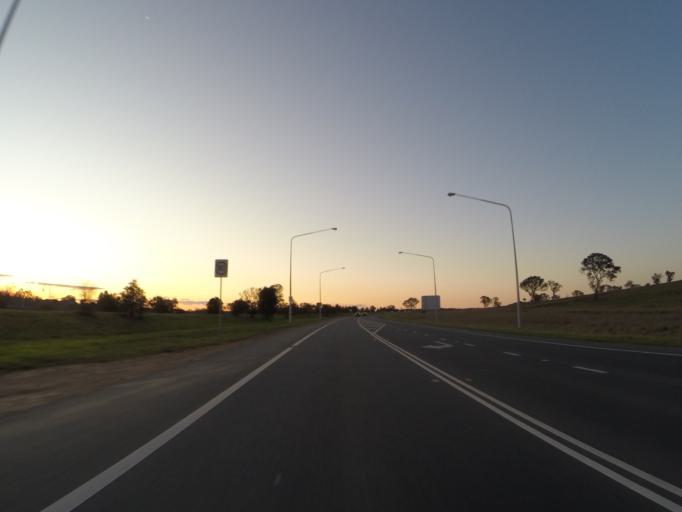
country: AU
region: Australian Capital Territory
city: Kaleen
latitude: -35.1999
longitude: 149.1649
